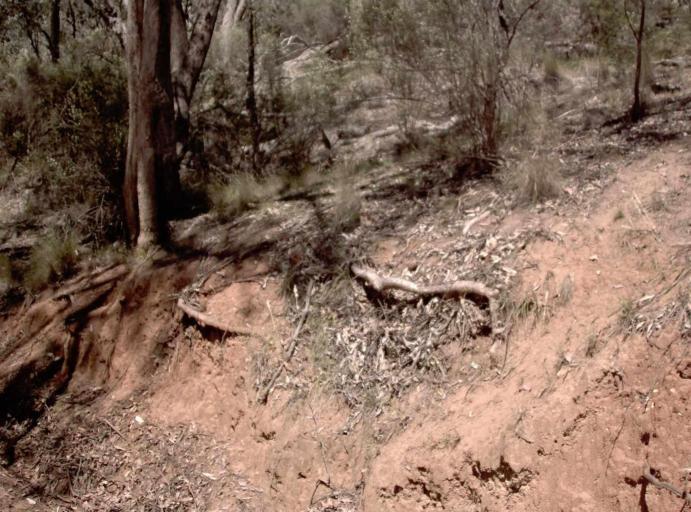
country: AU
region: New South Wales
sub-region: Snowy River
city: Jindabyne
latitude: -37.0538
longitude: 148.5385
